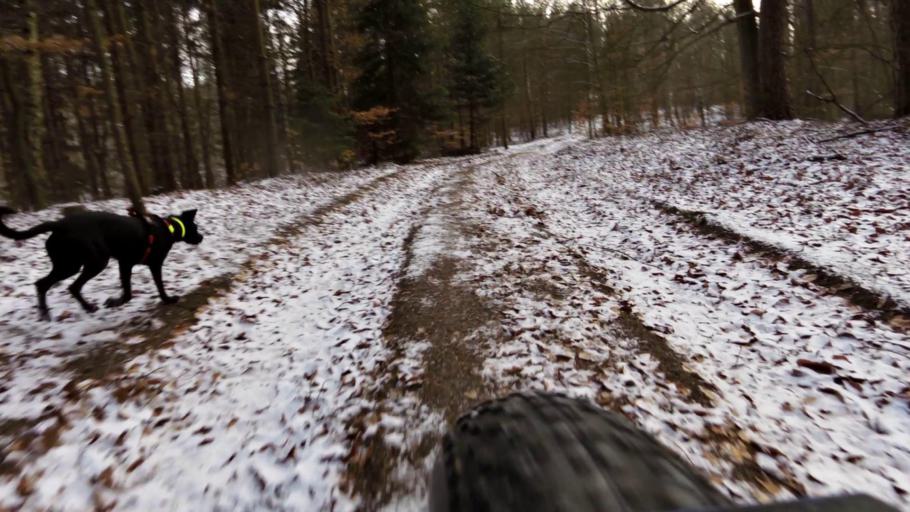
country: PL
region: West Pomeranian Voivodeship
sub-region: Powiat walecki
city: Tuczno
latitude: 53.2899
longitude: 16.2981
